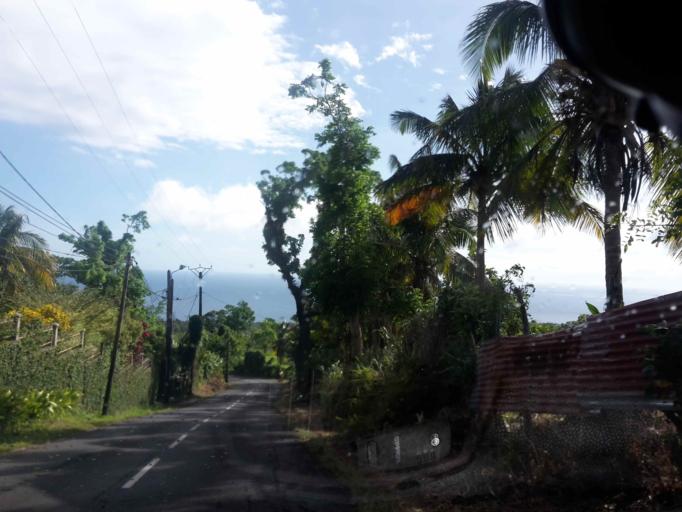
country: GP
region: Guadeloupe
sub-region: Guadeloupe
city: Gourbeyre
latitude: 16.0090
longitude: -61.6951
